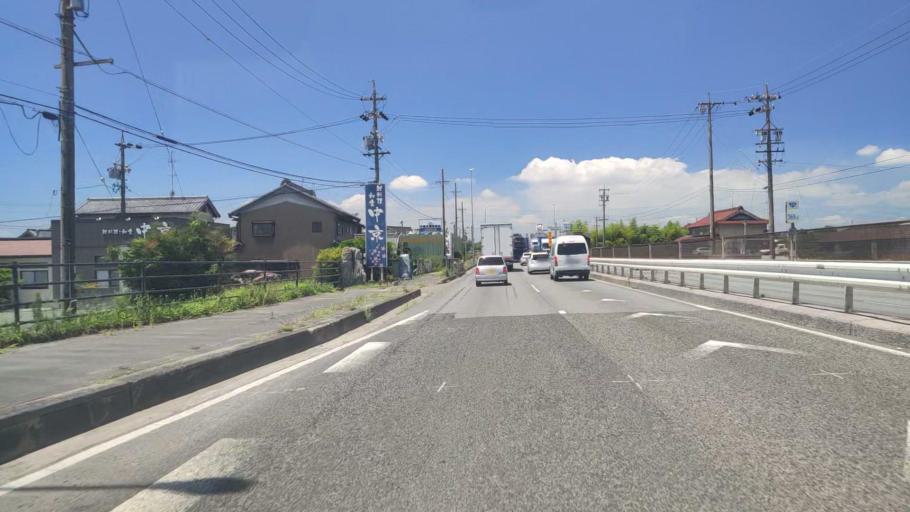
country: JP
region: Aichi
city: Kanie
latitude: 35.0769
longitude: 136.7834
